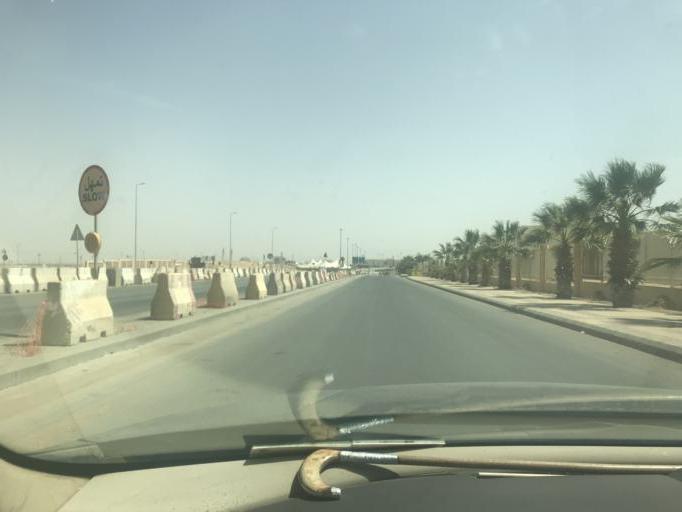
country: SA
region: Ar Riyad
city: Riyadh
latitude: 24.8273
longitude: 46.6957
